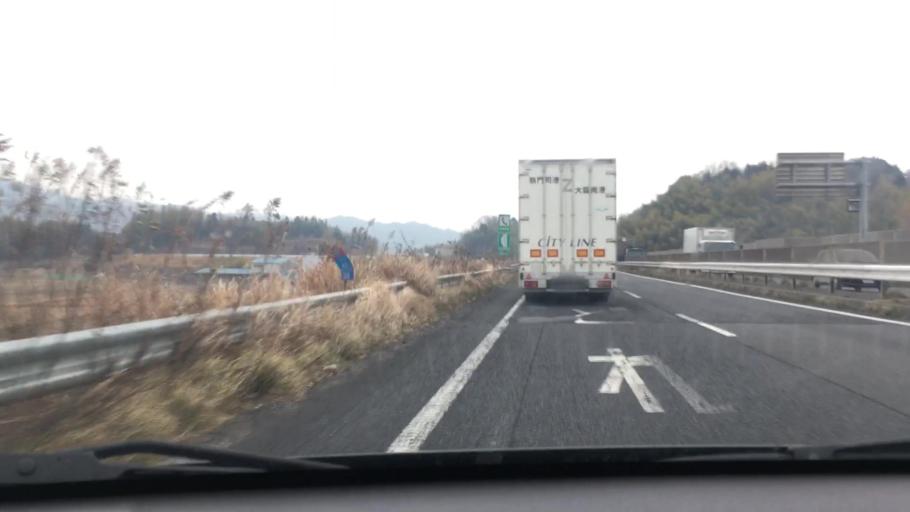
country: JP
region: Mie
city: Ueno-ebisumachi
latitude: 34.7819
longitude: 136.1586
